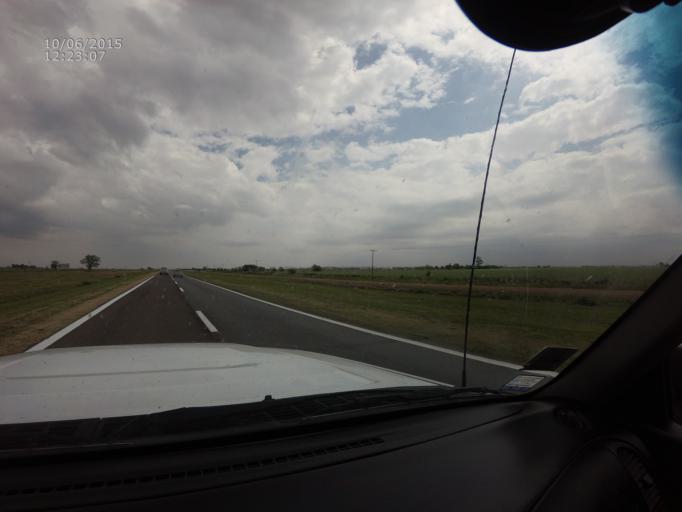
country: AR
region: Santa Fe
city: Roldan
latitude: -32.9154
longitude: -60.9505
